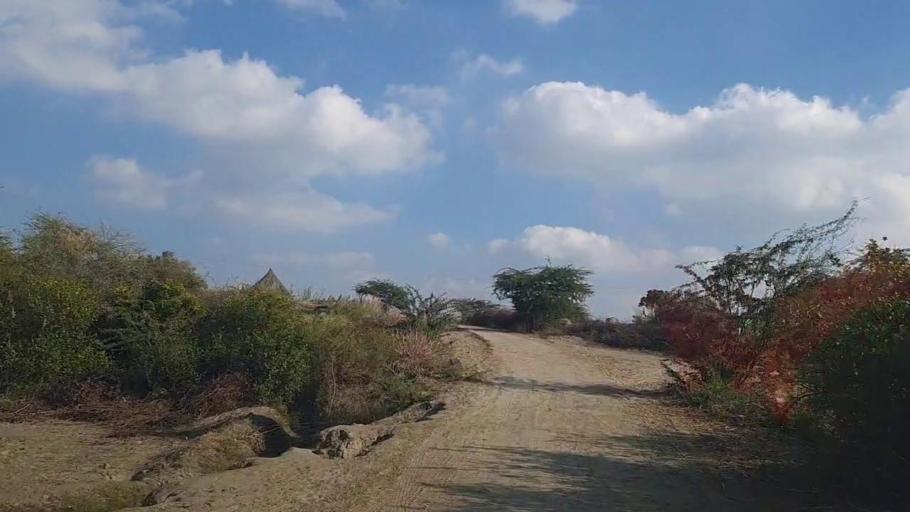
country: PK
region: Sindh
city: Tando Mittha Khan
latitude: 25.9886
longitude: 69.2464
